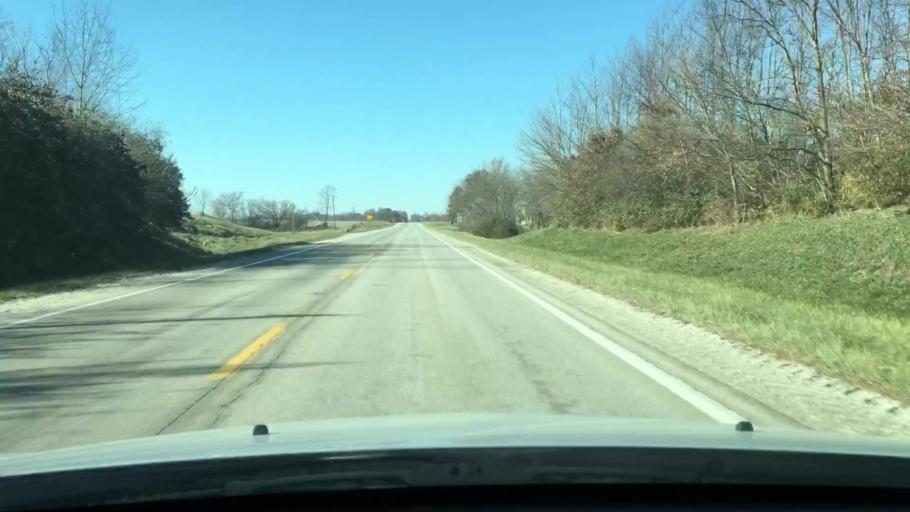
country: US
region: Illinois
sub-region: Pike County
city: Pittsfield
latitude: 39.6066
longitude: -90.7720
